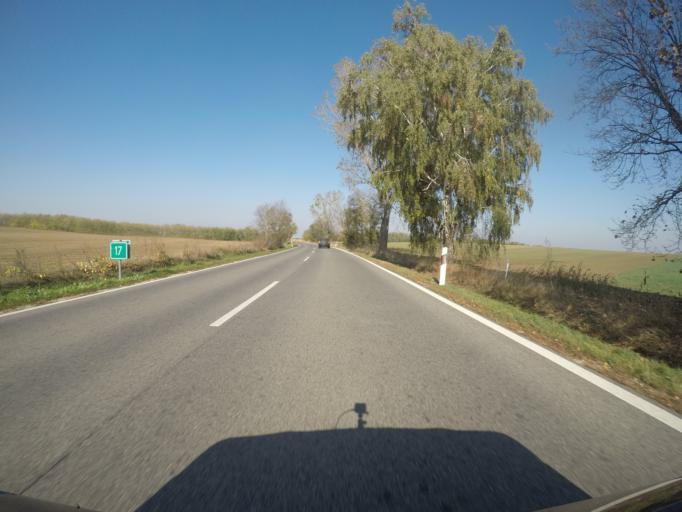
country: HU
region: Tolna
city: Tengelic
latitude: 46.5469
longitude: 18.6540
